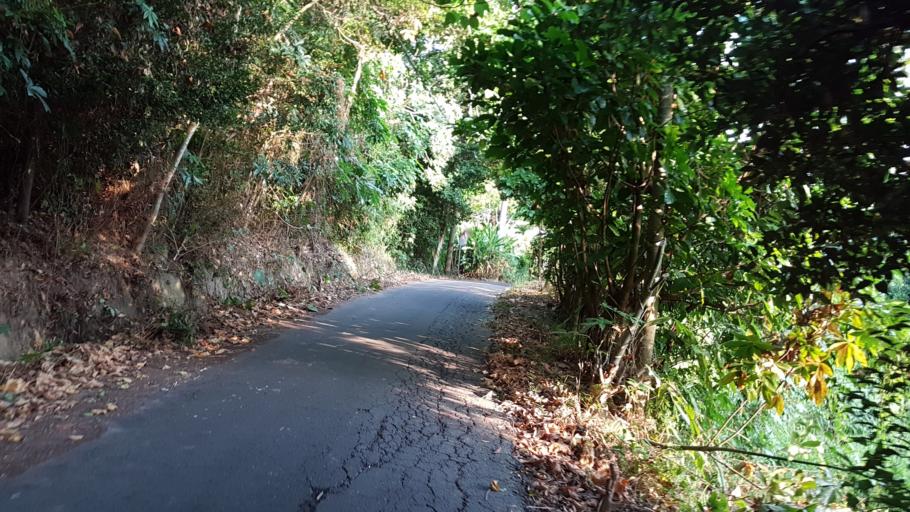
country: TW
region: Taiwan
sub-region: Chiayi
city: Jiayi Shi
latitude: 23.3671
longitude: 120.4640
